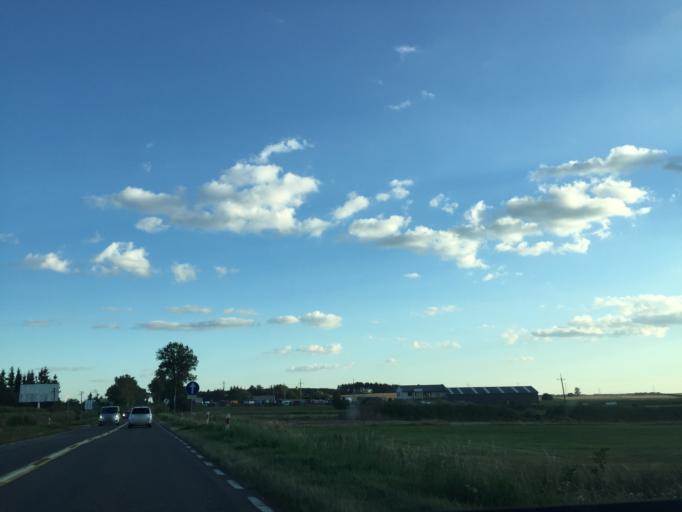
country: PL
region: Podlasie
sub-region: Lomza
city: Lomza
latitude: 53.1152
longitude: 22.0307
